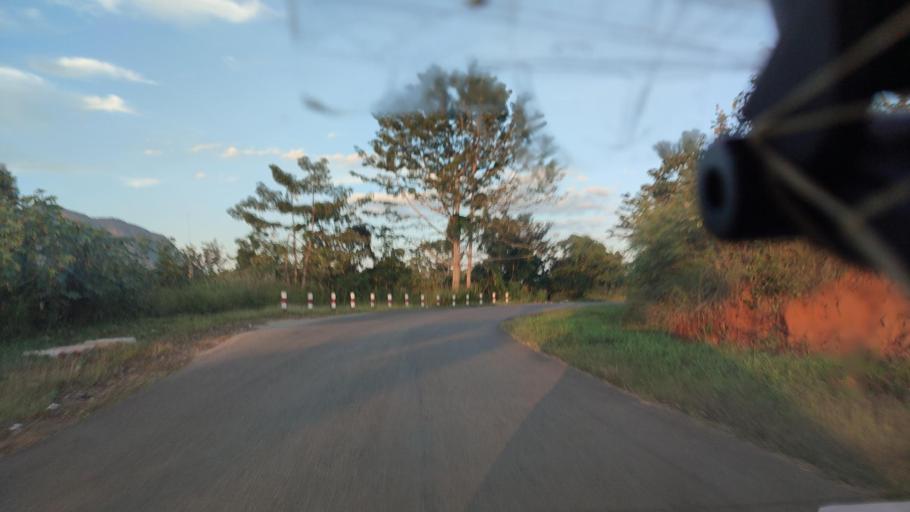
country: MM
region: Shan
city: Taunggyi
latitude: 20.9741
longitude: 97.8878
